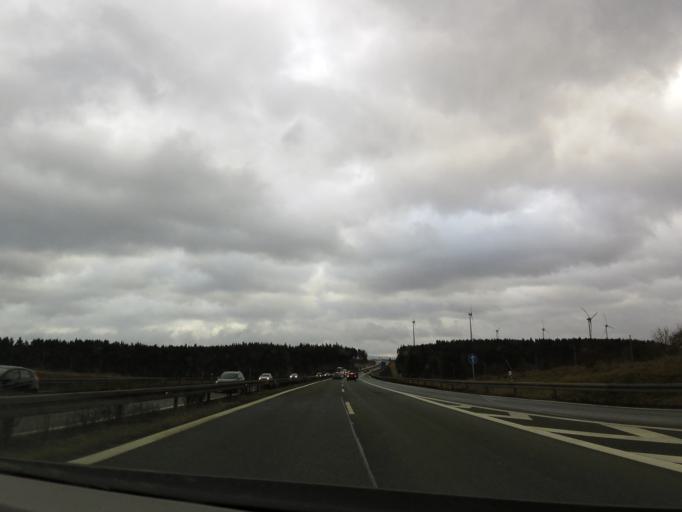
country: DE
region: Bavaria
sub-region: Upper Franconia
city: Gattendorf
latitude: 50.3220
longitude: 12.0238
